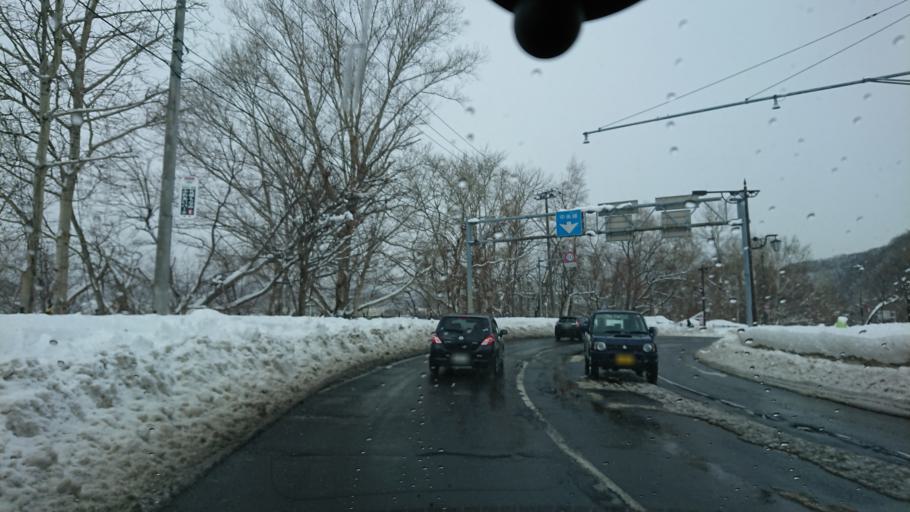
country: JP
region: Hokkaido
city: Sapporo
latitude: 42.9757
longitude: 141.3447
